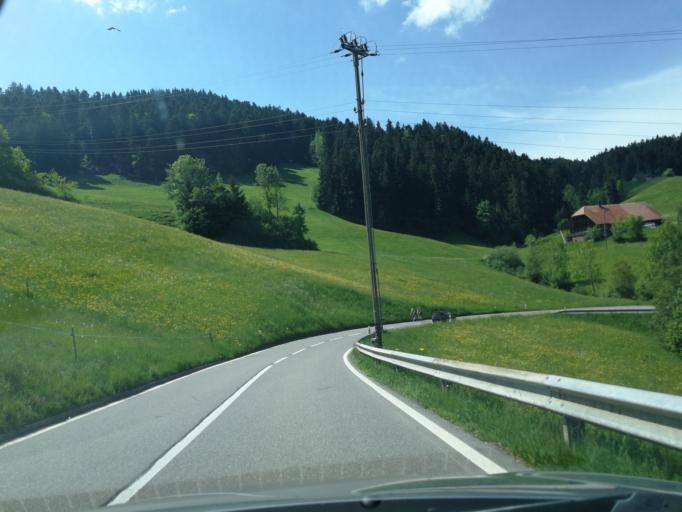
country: CH
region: Bern
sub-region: Bern-Mittelland District
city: Linden
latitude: 46.8385
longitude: 7.6535
